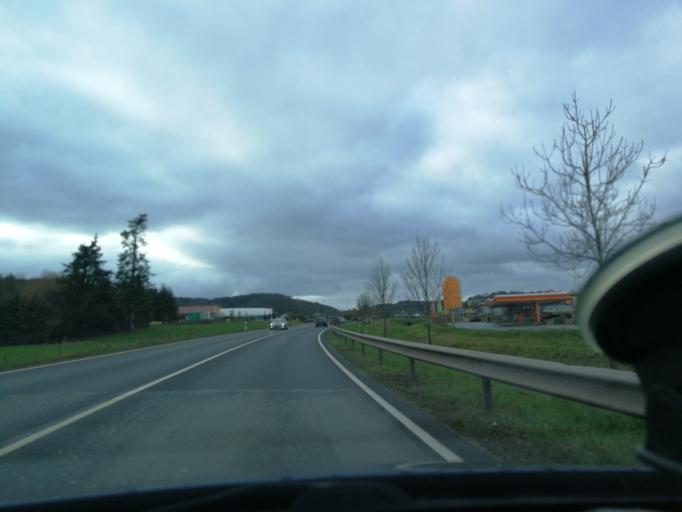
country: DE
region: Rheinland-Pfalz
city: Wittlich
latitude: 49.9763
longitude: 6.8922
